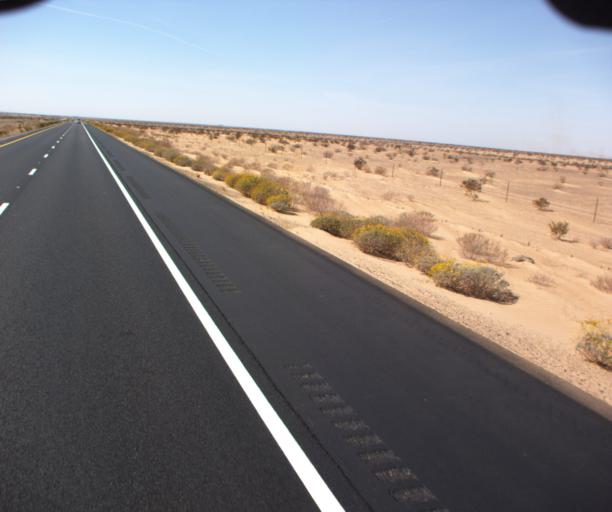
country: US
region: Arizona
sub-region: Yuma County
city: Somerton
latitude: 32.4954
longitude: -114.5919
